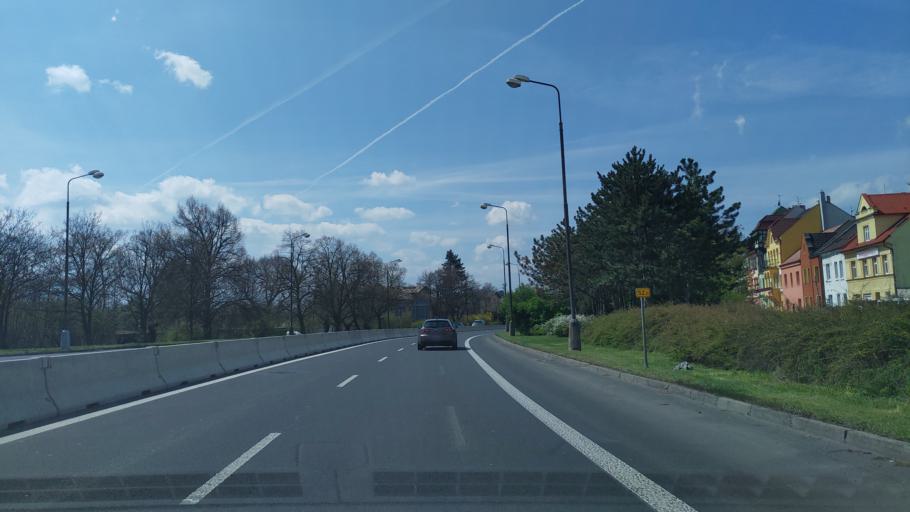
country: CZ
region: Ustecky
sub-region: Okres Chomutov
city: Chomutov
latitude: 50.4600
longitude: 13.4027
